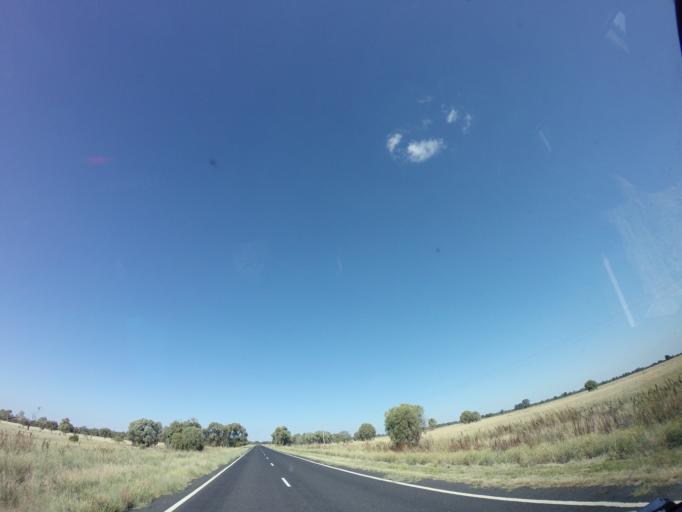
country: AU
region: New South Wales
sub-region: Gilgandra
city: Gilgandra
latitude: -31.6654
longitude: 148.1712
